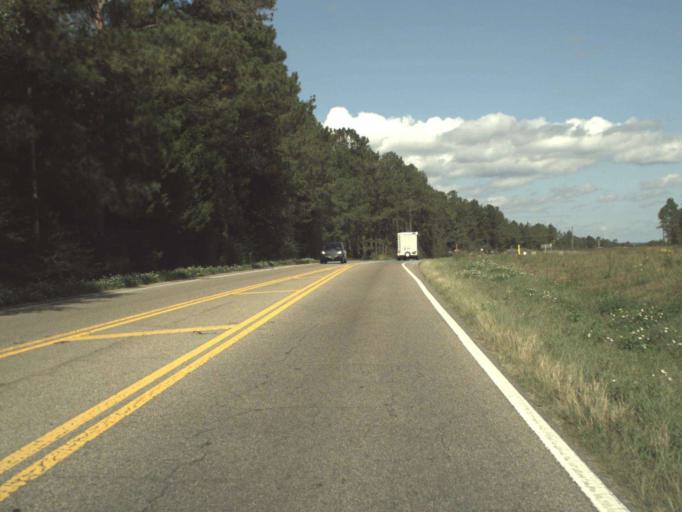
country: US
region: Florida
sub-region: Walton County
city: DeFuniak Springs
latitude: 30.6609
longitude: -86.1206
